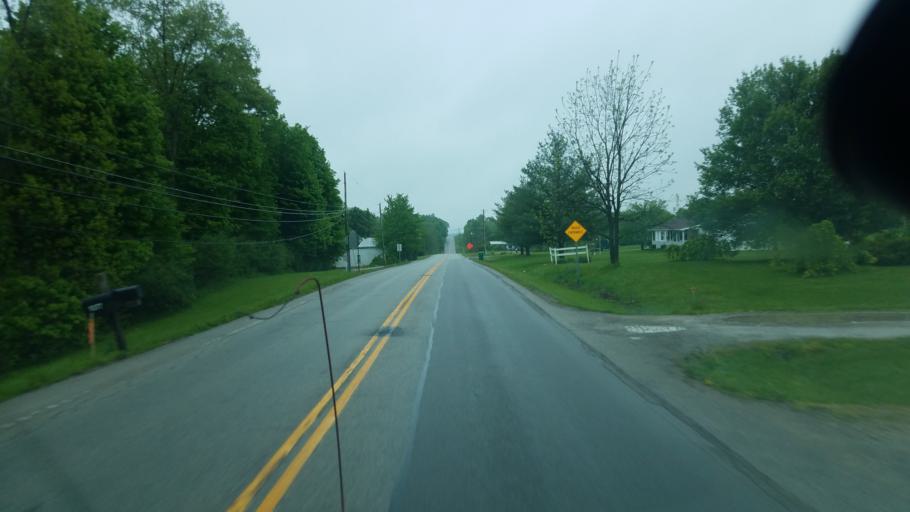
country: US
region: Ohio
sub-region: Highland County
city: Hillsboro
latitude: 39.2684
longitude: -83.5976
